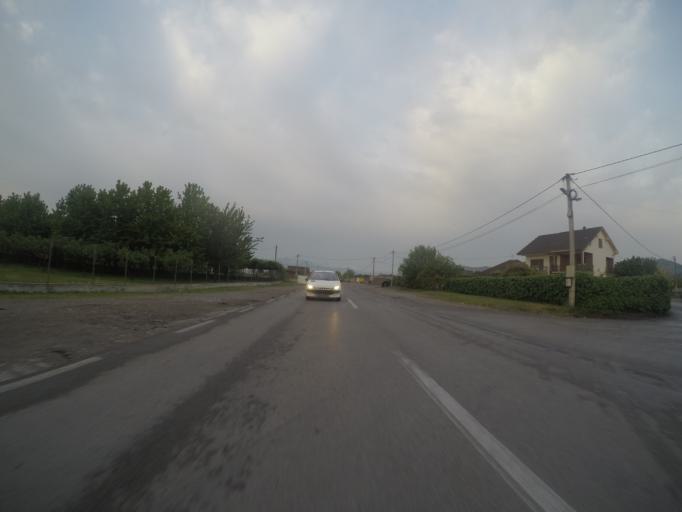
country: ME
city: Golubovci
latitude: 42.3253
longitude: 19.2185
